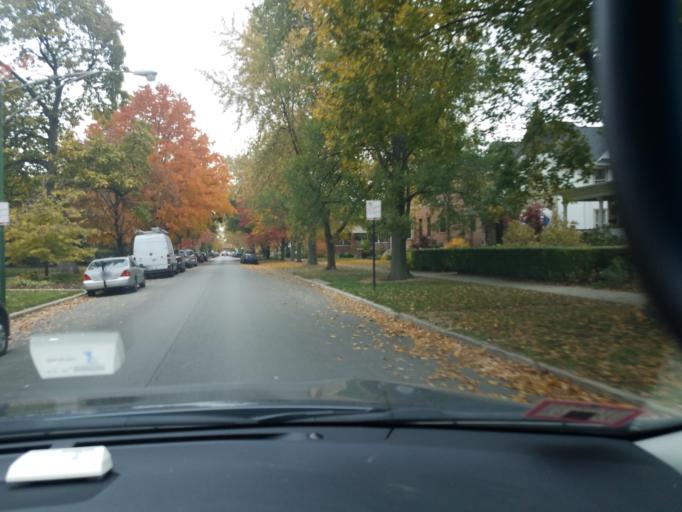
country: US
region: Illinois
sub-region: Cook County
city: Lincolnwood
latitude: 41.9508
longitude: -87.7324
